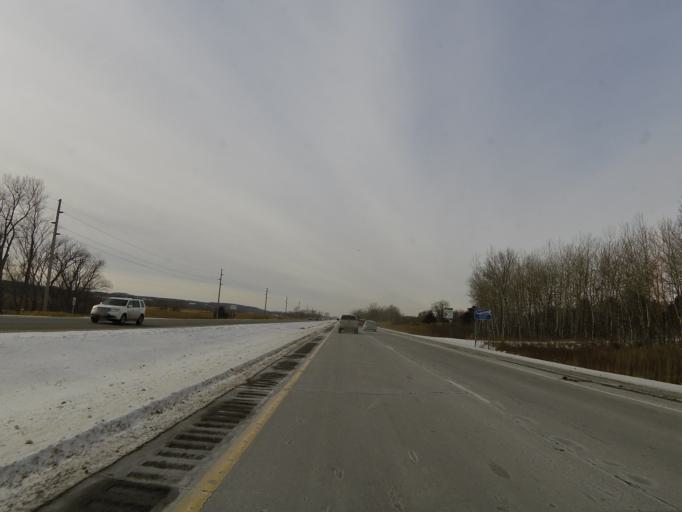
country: US
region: Minnesota
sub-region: Scott County
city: Jordan
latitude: 44.6663
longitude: -93.6513
